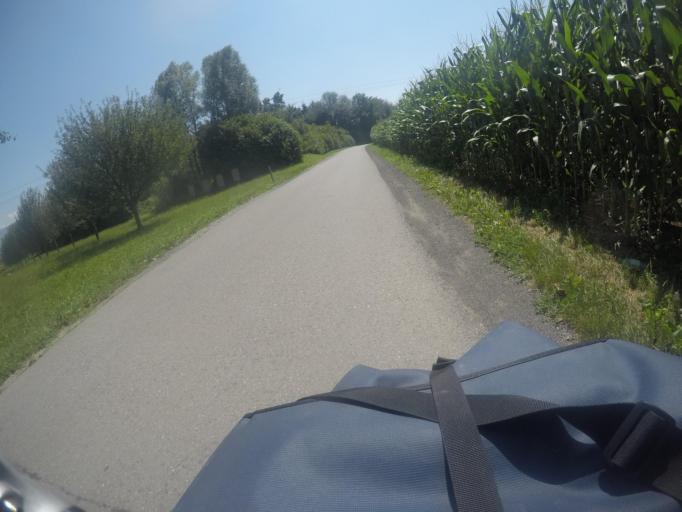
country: CH
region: Saint Gallen
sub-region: Wahlkreis Rheintal
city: Rebstein
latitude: 47.3870
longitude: 9.5714
